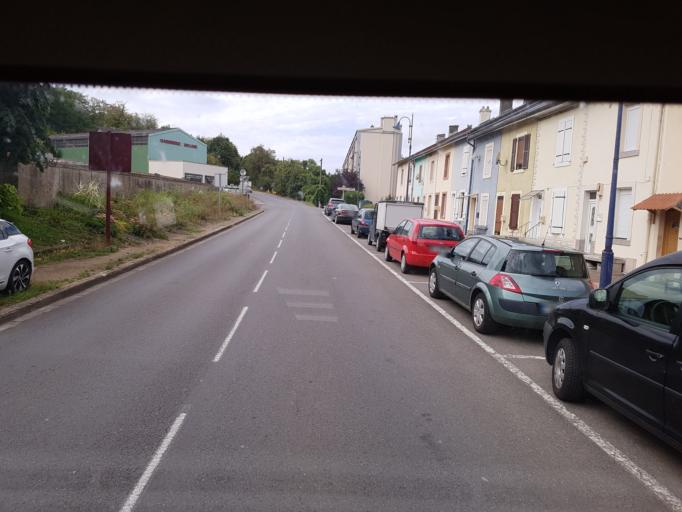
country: FR
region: Lorraine
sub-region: Departement de la Moselle
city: Moyeuvre-Grande
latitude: 49.2442
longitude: 6.0330
